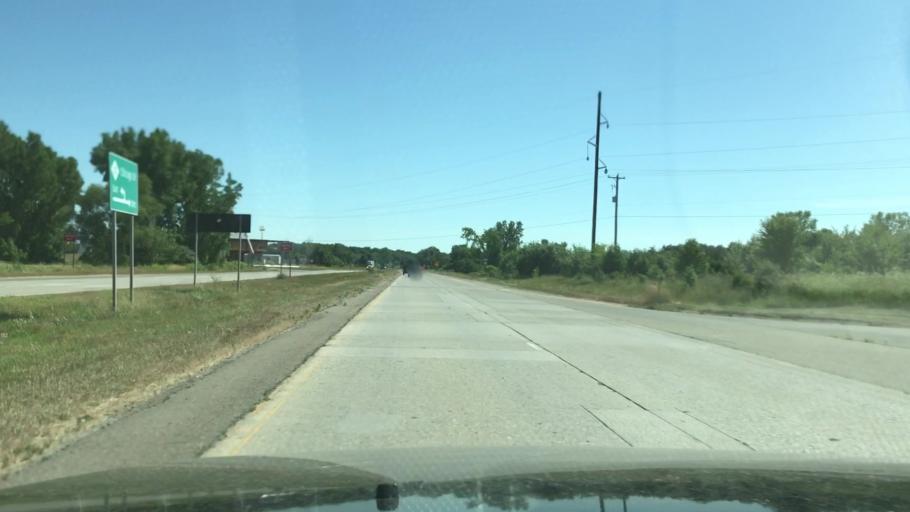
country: US
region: Michigan
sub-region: Ottawa County
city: Zeeland
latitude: 42.8178
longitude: -85.9889
